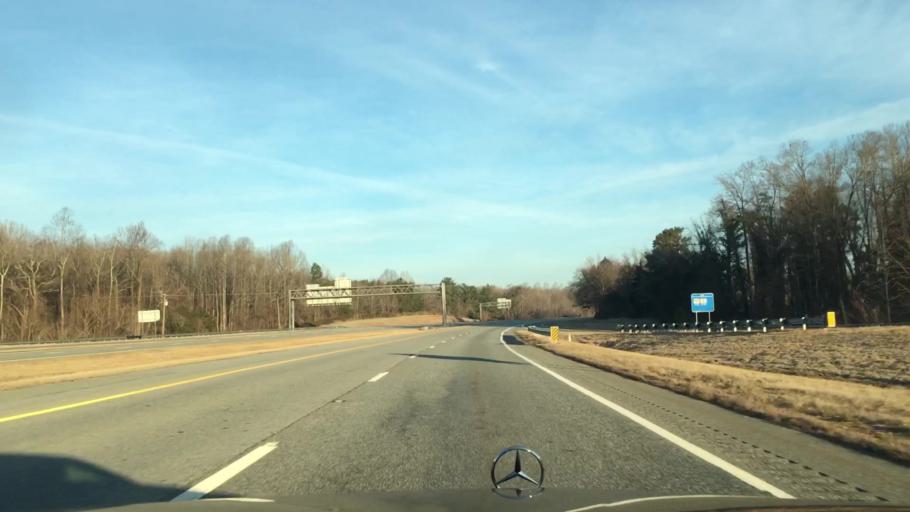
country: US
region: North Carolina
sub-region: Guilford County
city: Pleasant Garden
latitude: 36.0014
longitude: -79.7547
